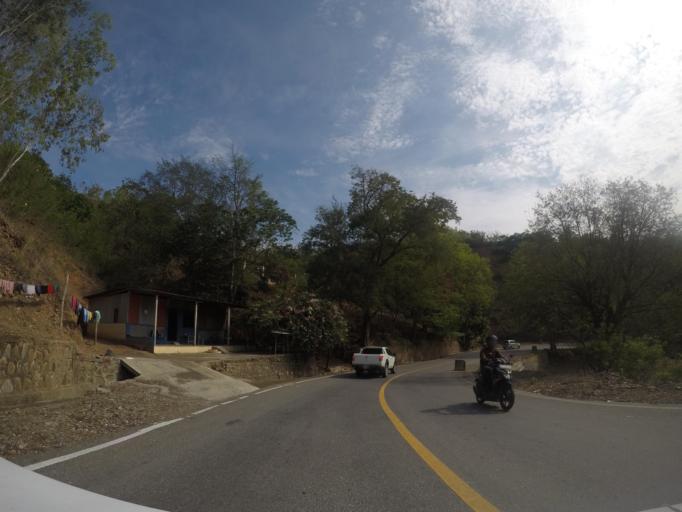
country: TL
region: Dili
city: Dili
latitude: -8.5573
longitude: 125.6440
